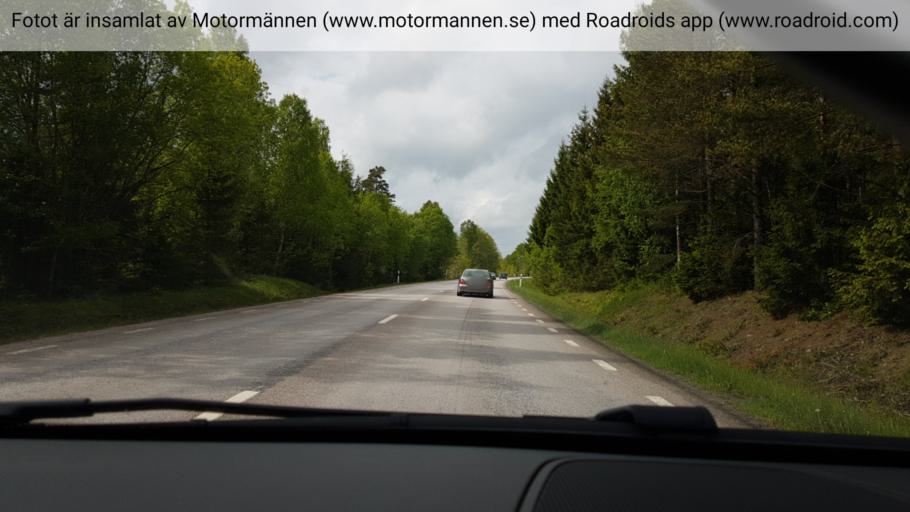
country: SE
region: Uppsala
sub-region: Osthammars Kommun
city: Osterbybruk
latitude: 60.1750
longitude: 17.9207
